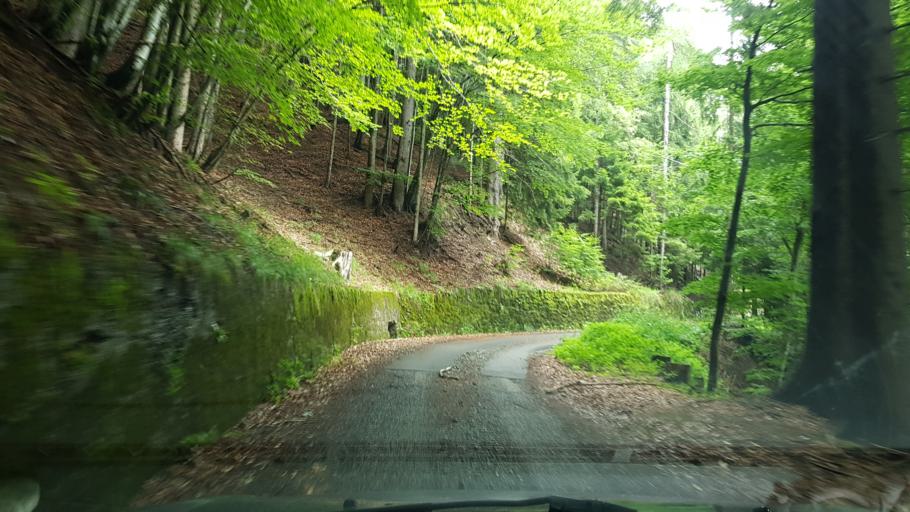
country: IT
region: Friuli Venezia Giulia
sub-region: Provincia di Udine
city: Cercivento
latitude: 46.5383
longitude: 12.9882
